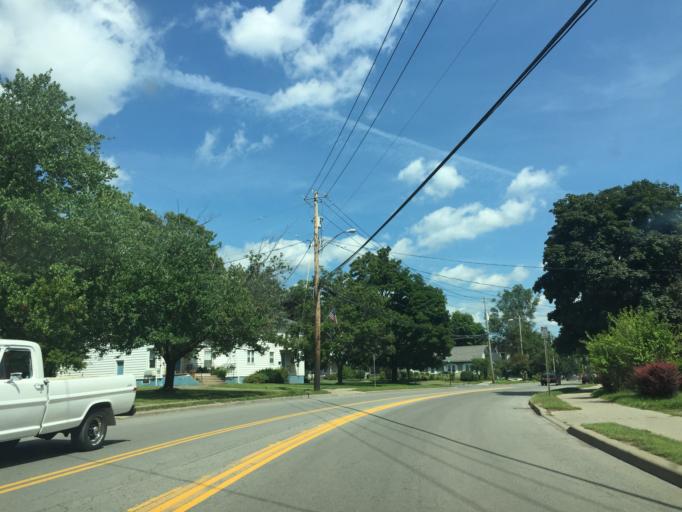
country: US
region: New York
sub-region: Delaware County
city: Delhi
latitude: 42.2735
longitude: -74.9218
